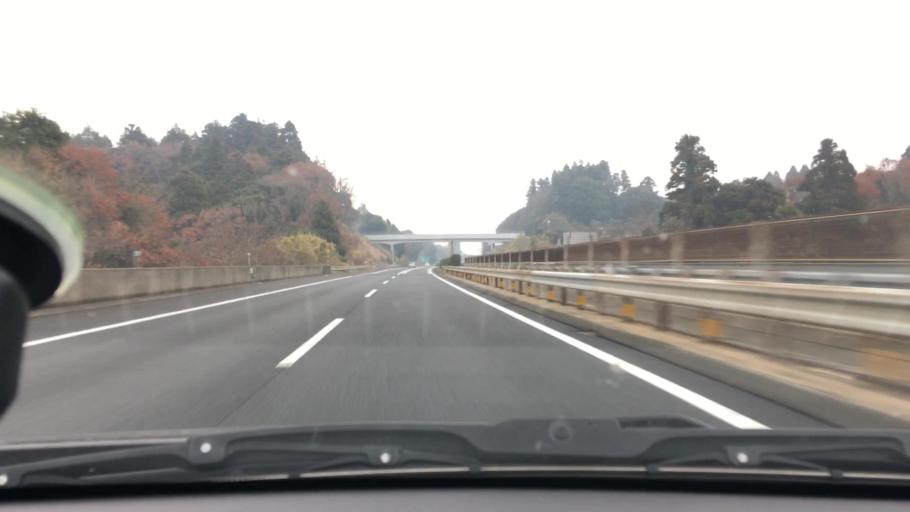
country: JP
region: Chiba
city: Narita
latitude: 35.7943
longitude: 140.3525
